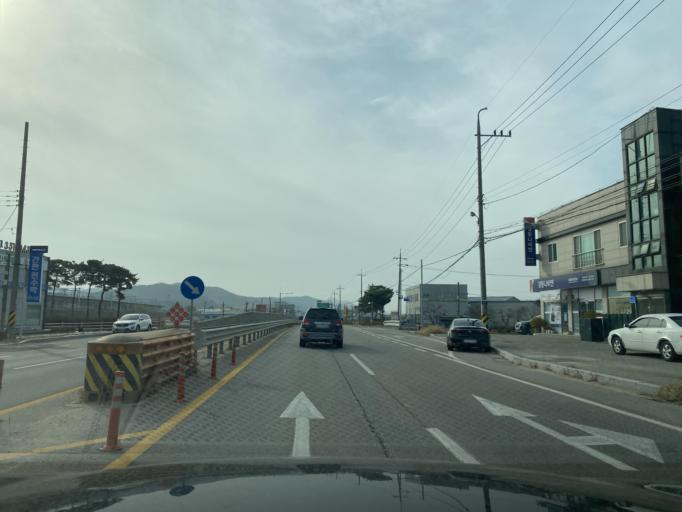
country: KR
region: Chungcheongnam-do
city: Yesan
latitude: 36.6897
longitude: 126.8275
